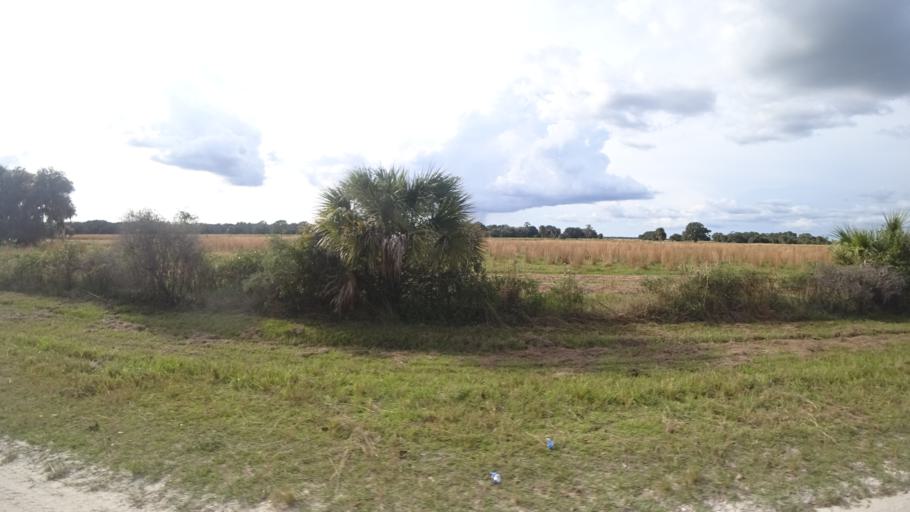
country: US
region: Florida
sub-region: Sarasota County
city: Warm Mineral Springs
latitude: 27.2454
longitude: -82.1662
